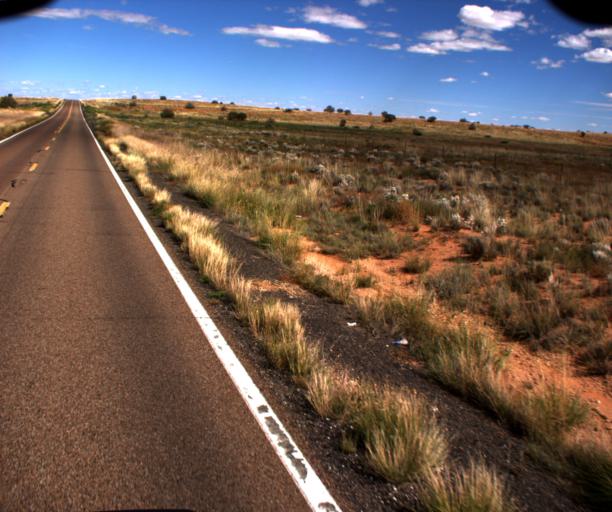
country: US
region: Arizona
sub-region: Navajo County
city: Holbrook
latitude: 34.7495
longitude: -110.2600
